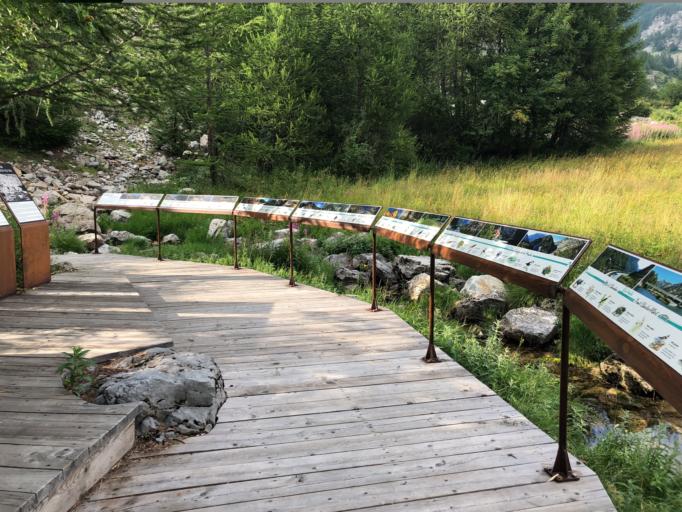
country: FR
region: Provence-Alpes-Cote d'Azur
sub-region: Departement des Alpes-de-Haute-Provence
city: Barcelonnette
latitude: 44.2385
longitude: 6.7515
